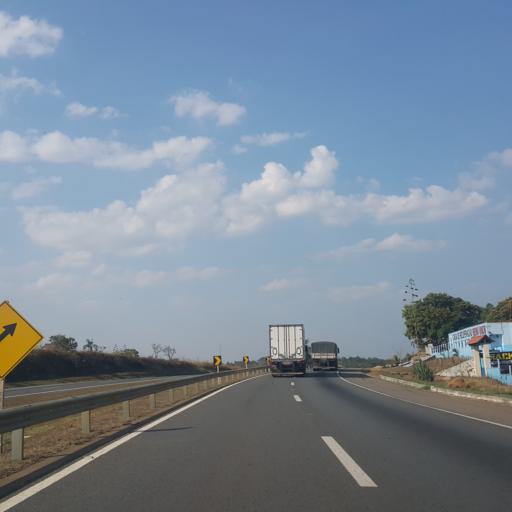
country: BR
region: Goias
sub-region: Abadiania
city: Abadiania
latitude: -16.1729
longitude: -48.6470
